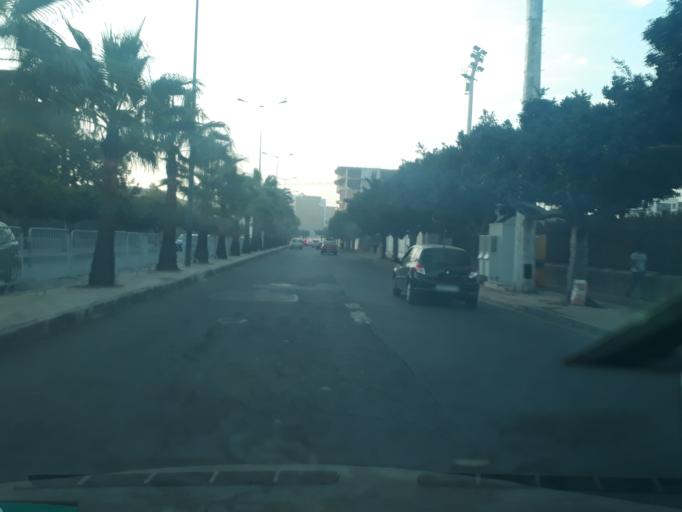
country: MA
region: Grand Casablanca
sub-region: Casablanca
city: Casablanca
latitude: 33.5828
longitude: -7.6488
